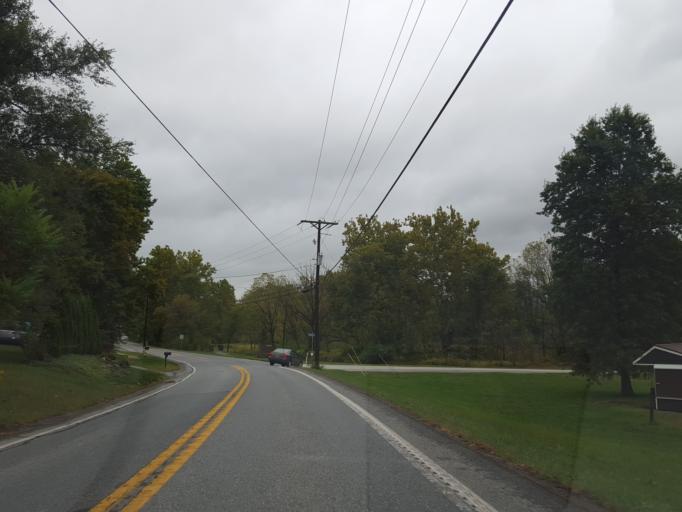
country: US
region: Pennsylvania
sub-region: York County
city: Spry
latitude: 39.9453
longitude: -76.6626
